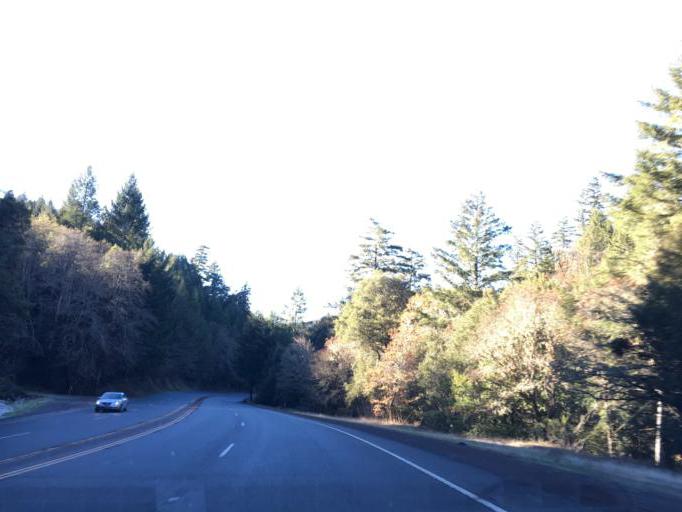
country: US
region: California
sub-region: Mendocino County
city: Laytonville
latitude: 39.8305
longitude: -123.6144
